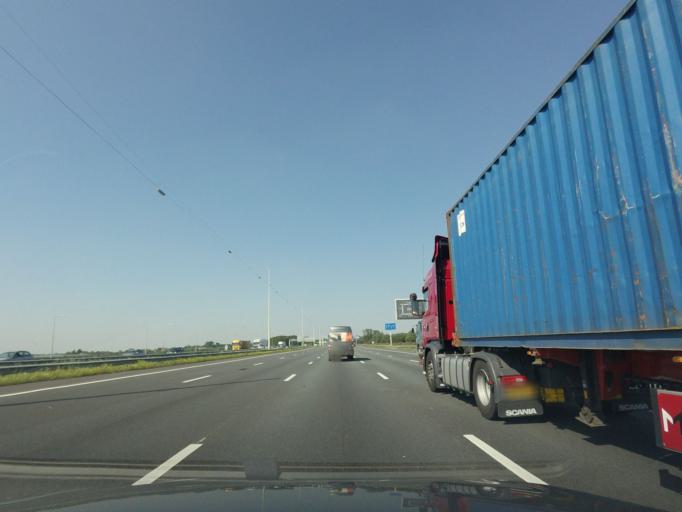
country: NL
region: South Holland
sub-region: Gemeente Hendrik-Ido-Ambacht
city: Hendrik-Ido-Ambacht
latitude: 51.8399
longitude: 4.6143
